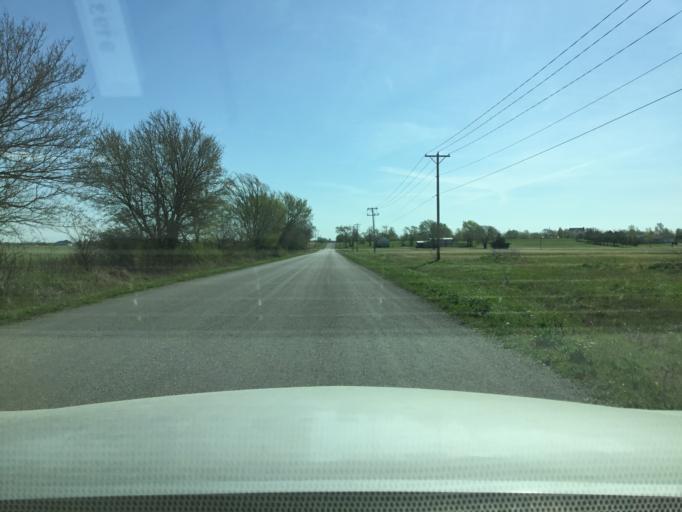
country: US
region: Kansas
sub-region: Neosho County
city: Chanute
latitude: 37.6458
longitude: -95.4471
